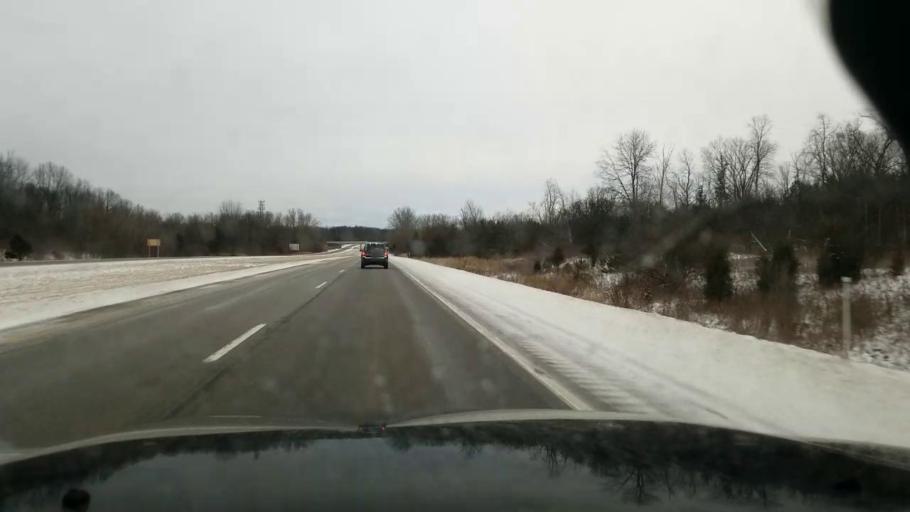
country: US
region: Michigan
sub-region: Jackson County
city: Jackson
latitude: 42.2393
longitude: -84.4756
